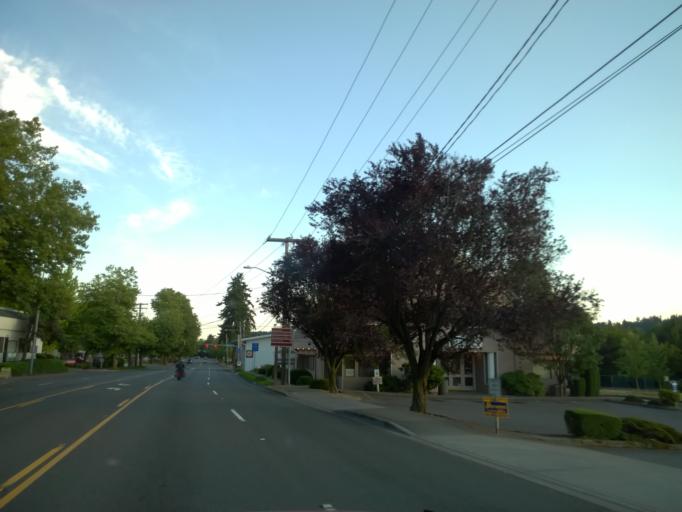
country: US
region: Washington
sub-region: King County
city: Woodinville
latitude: 47.7561
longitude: -122.1528
